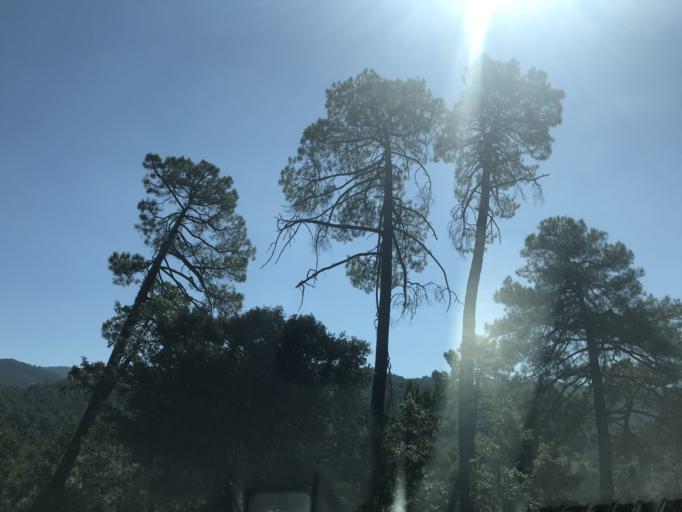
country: ES
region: Andalusia
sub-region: Provincia de Jaen
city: La Iruela
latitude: 37.9202
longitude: -2.9325
